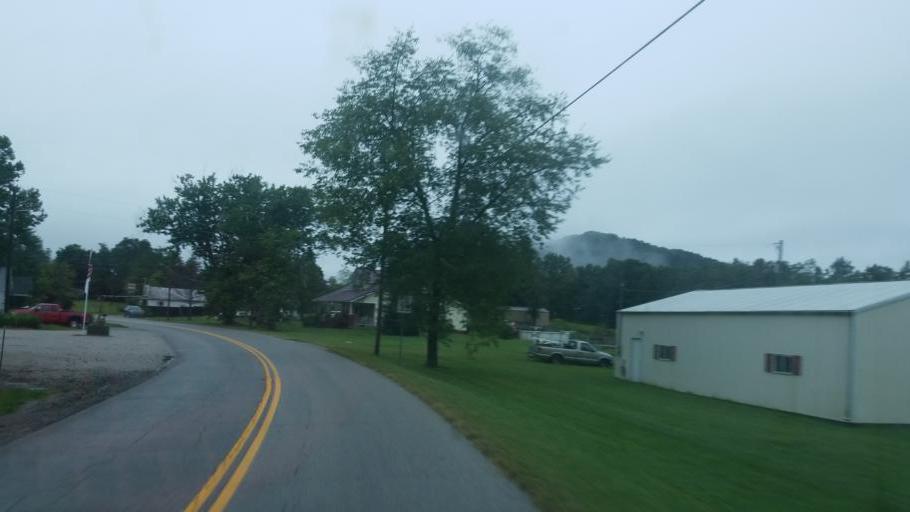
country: US
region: Kentucky
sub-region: Fleming County
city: Flemingsburg
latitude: 38.4050
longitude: -83.6111
